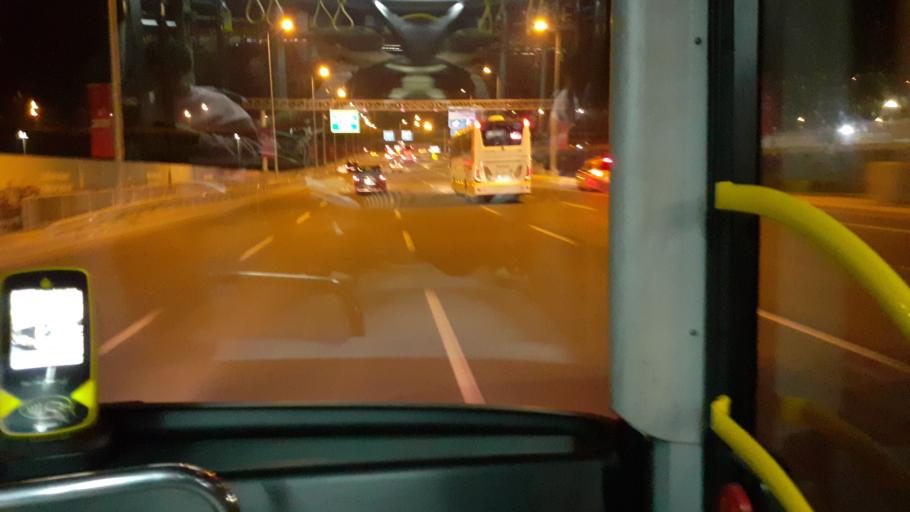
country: TR
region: Istanbul
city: Durusu
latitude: 41.2498
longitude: 28.7389
